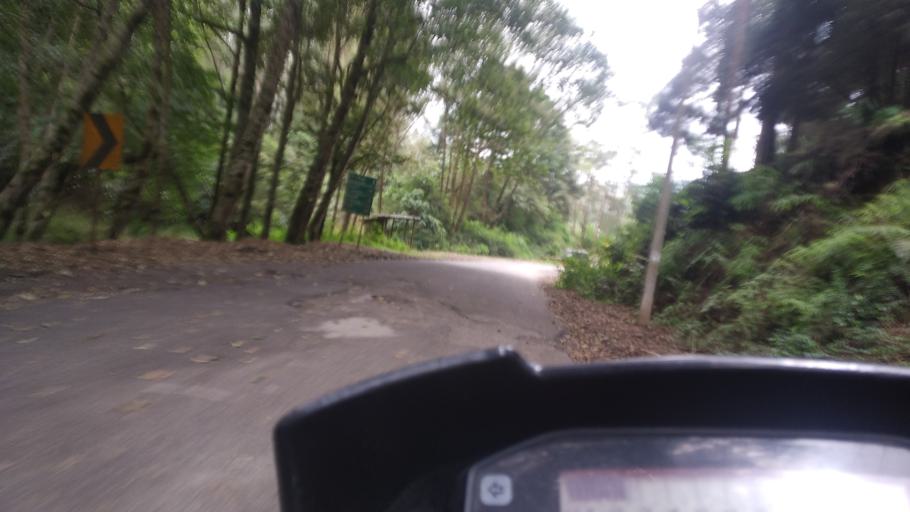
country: IN
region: Kerala
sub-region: Idukki
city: Munnar
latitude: 10.0656
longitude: 77.0999
